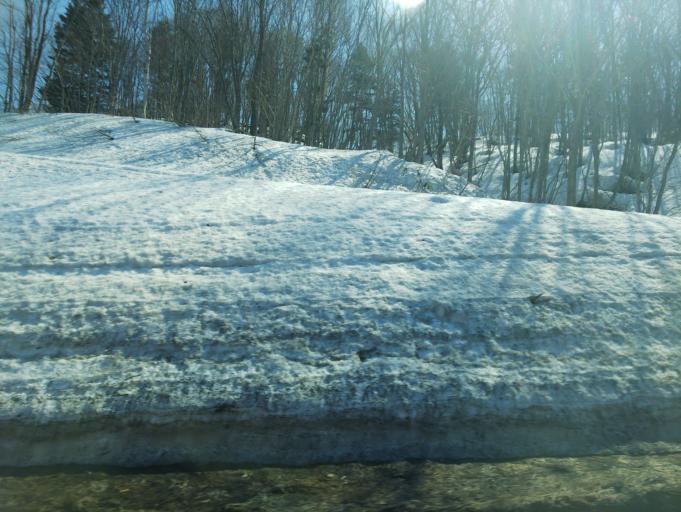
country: JP
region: Hokkaido
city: Nayoro
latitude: 44.7029
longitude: 142.2737
